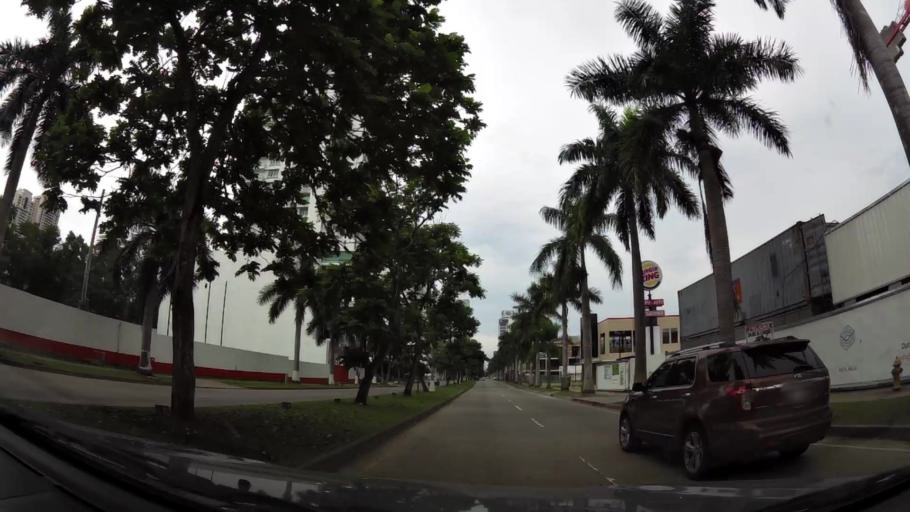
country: PA
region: Panama
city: San Miguelito
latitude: 9.0162
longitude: -79.4707
